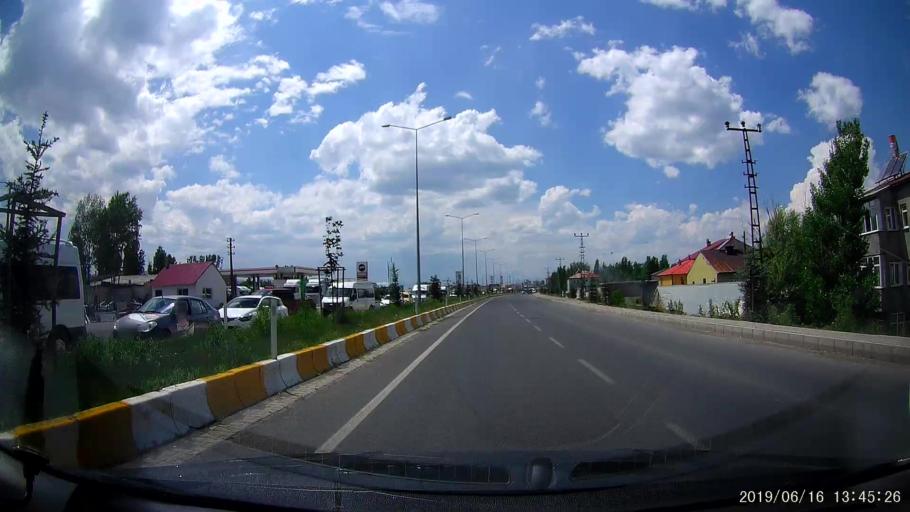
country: TR
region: Agri
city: Agri
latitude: 39.7087
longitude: 43.0459
